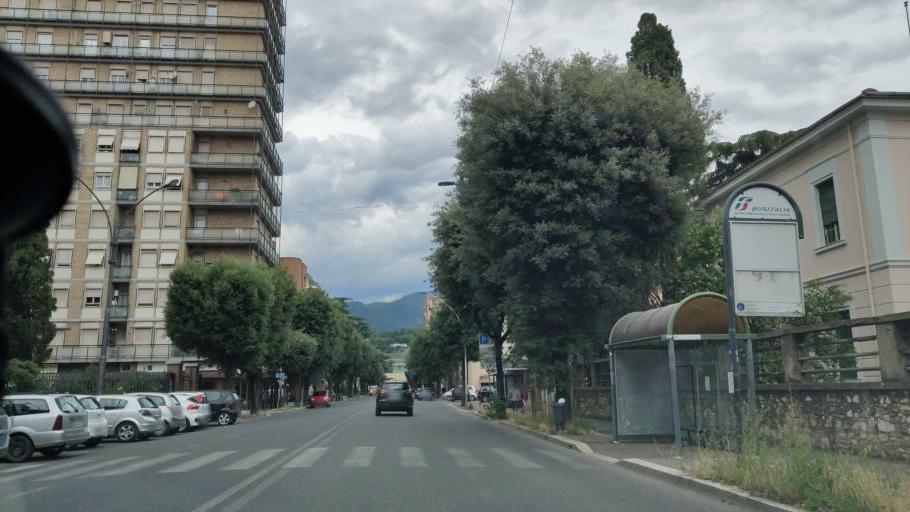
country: IT
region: Umbria
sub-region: Provincia di Terni
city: Terni
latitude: 42.5674
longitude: 12.6531
